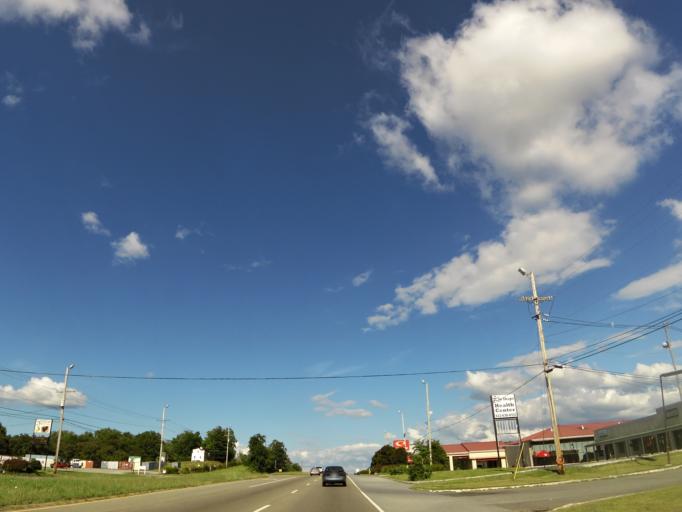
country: US
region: Tennessee
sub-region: Greene County
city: Tusculum
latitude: 36.1772
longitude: -82.7930
